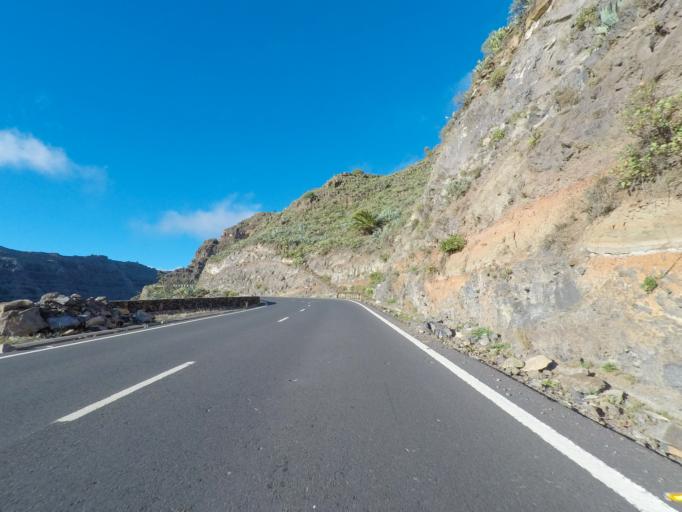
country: ES
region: Canary Islands
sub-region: Provincia de Santa Cruz de Tenerife
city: Vallehermosa
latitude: 28.1169
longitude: -17.3203
